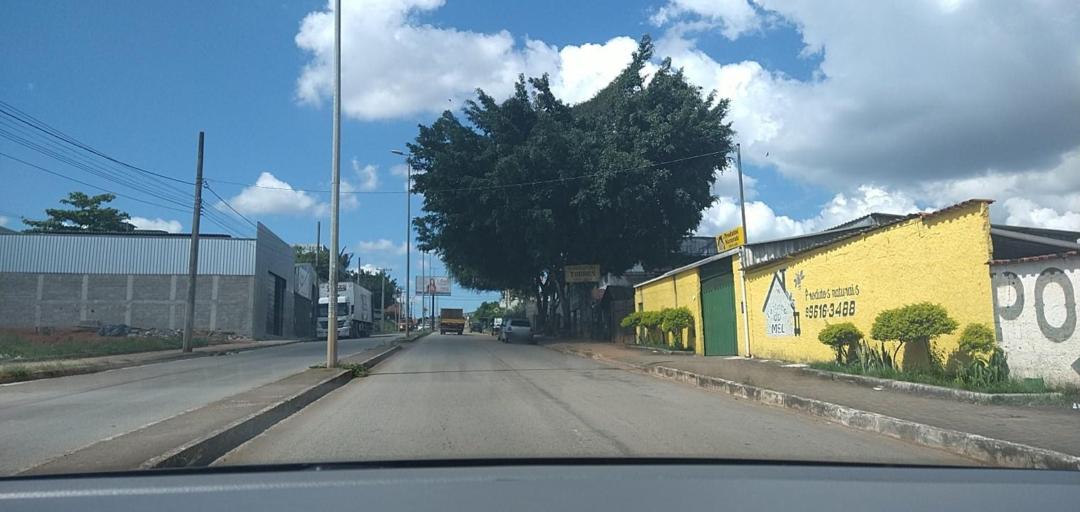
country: BR
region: Minas Gerais
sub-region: Joao Monlevade
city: Joao Monlevade
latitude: -19.8350
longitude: -43.1907
